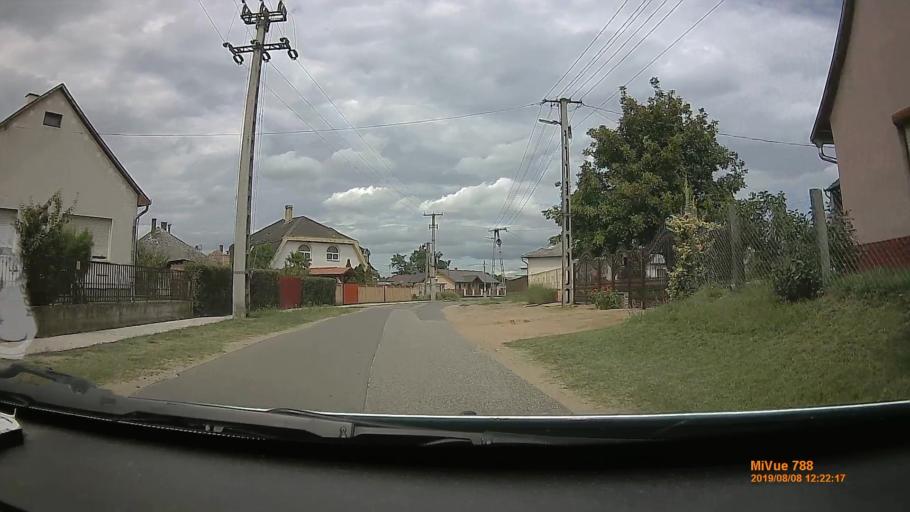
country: HU
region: Szabolcs-Szatmar-Bereg
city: Nyirbogat
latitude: 47.7987
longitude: 22.0541
